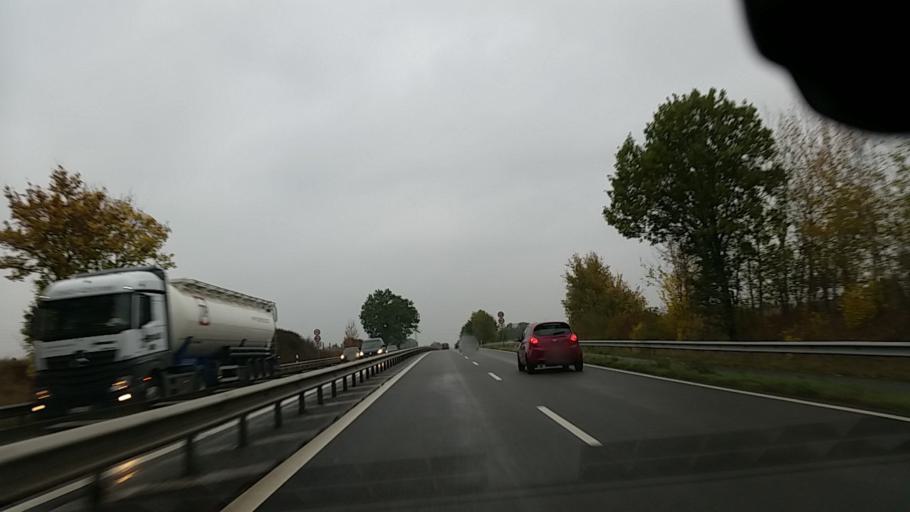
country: DE
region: Lower Saxony
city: Melbeck
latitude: 53.1926
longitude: 10.4052
